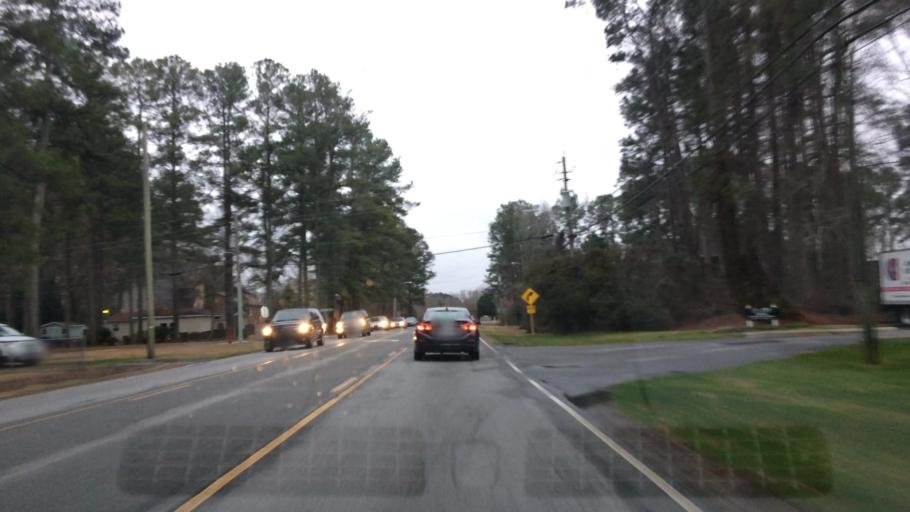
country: US
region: North Carolina
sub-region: Pitt County
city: Summerfield
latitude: 35.5698
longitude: -77.3828
